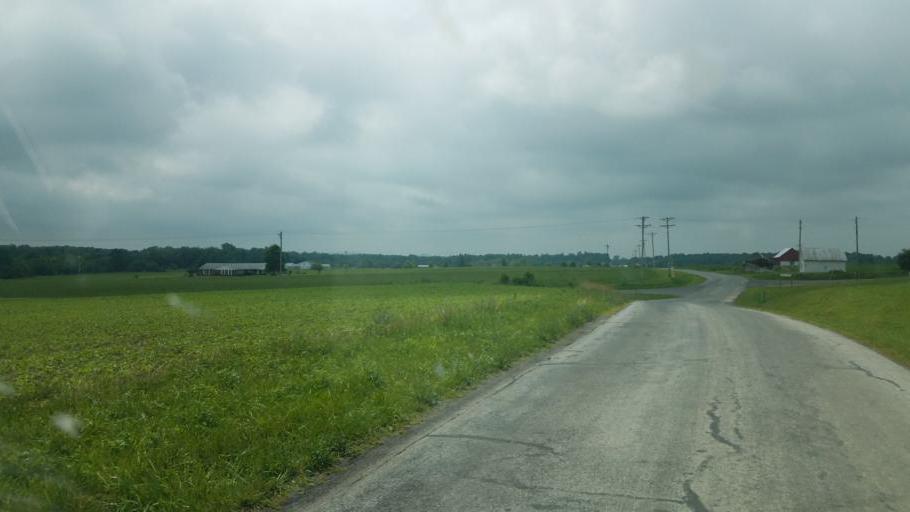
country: US
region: Ohio
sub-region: Highland County
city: Leesburg
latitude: 39.2360
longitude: -83.4879
